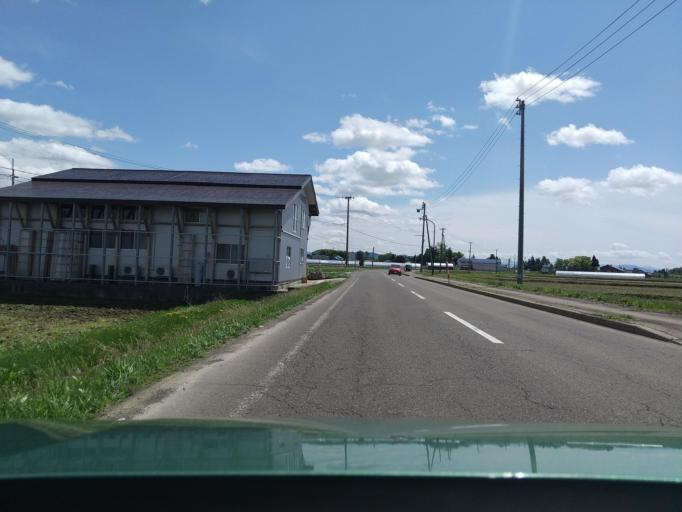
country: JP
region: Akita
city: Yokotemachi
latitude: 39.3610
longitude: 140.5377
